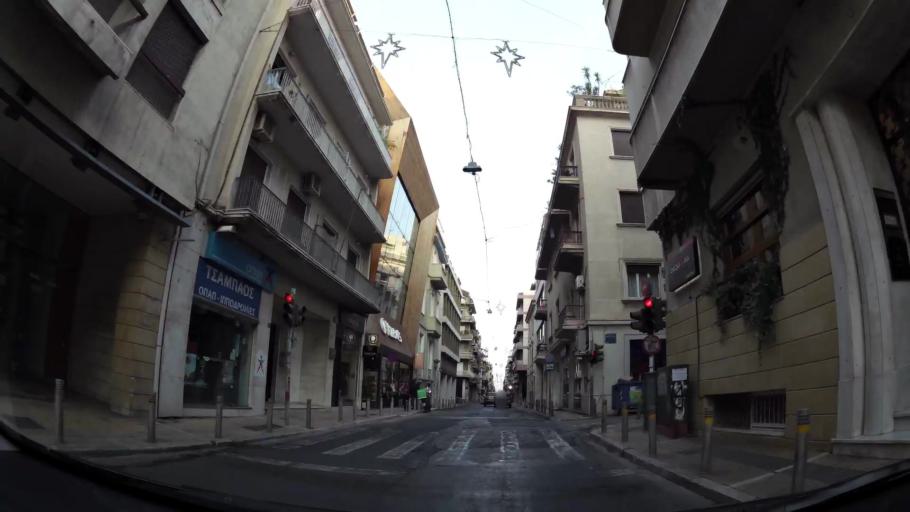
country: GR
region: Attica
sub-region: Nomarchia Athinas
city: Vyronas
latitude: 37.9774
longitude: 23.7391
